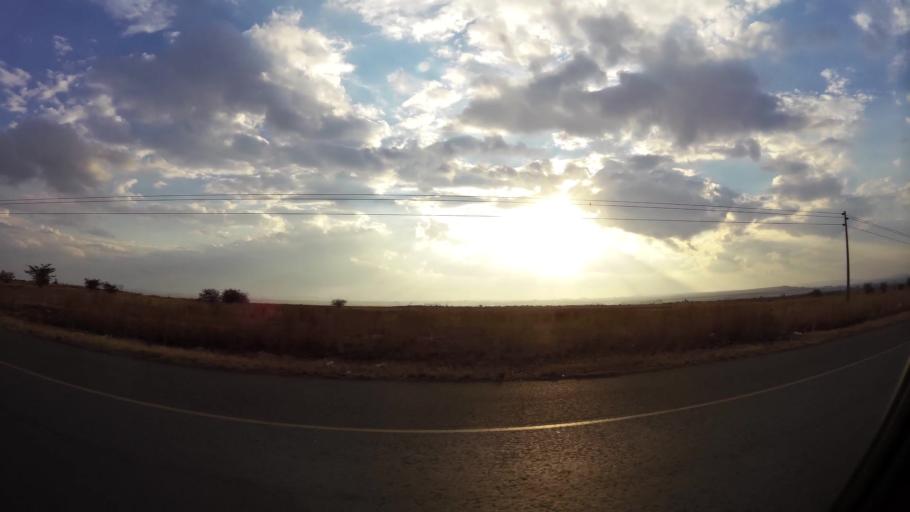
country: ZA
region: Gauteng
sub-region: Sedibeng District Municipality
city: Vanderbijlpark
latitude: -26.5940
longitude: 27.8204
